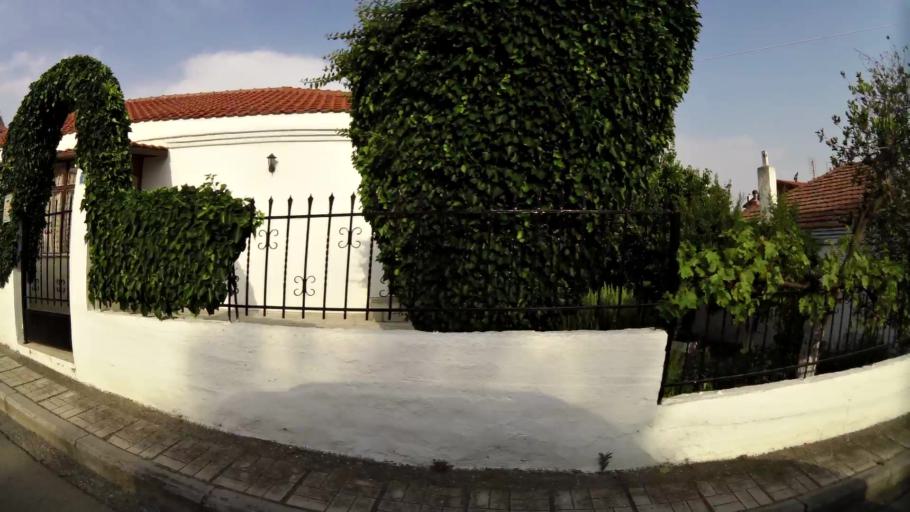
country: GR
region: Central Macedonia
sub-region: Nomos Thessalonikis
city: Oraiokastro
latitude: 40.7243
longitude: 22.9060
